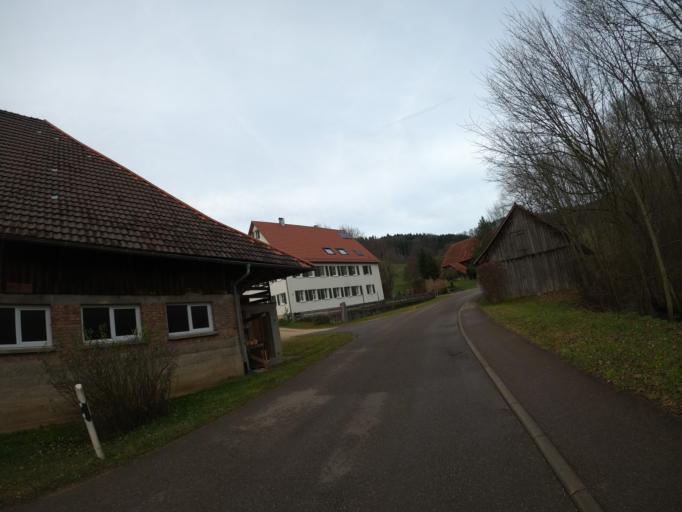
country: DE
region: Baden-Wuerttemberg
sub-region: Regierungsbezirk Stuttgart
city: Ottenbach
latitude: 48.7455
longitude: 9.7539
